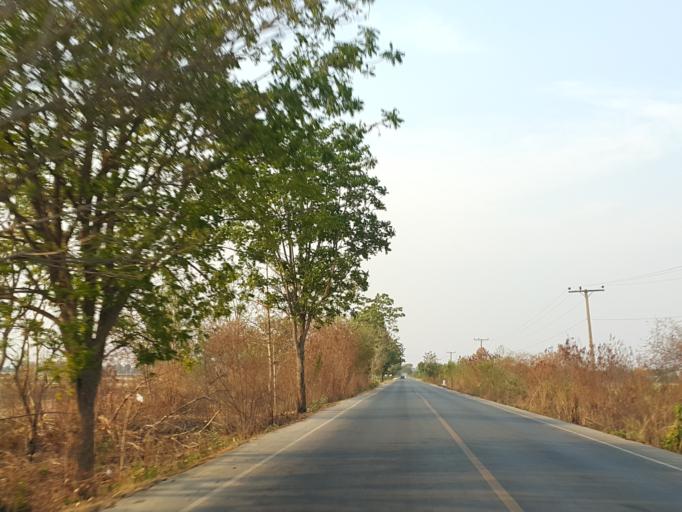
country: TH
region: Sukhothai
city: Si Samrong
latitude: 17.2209
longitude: 99.9515
